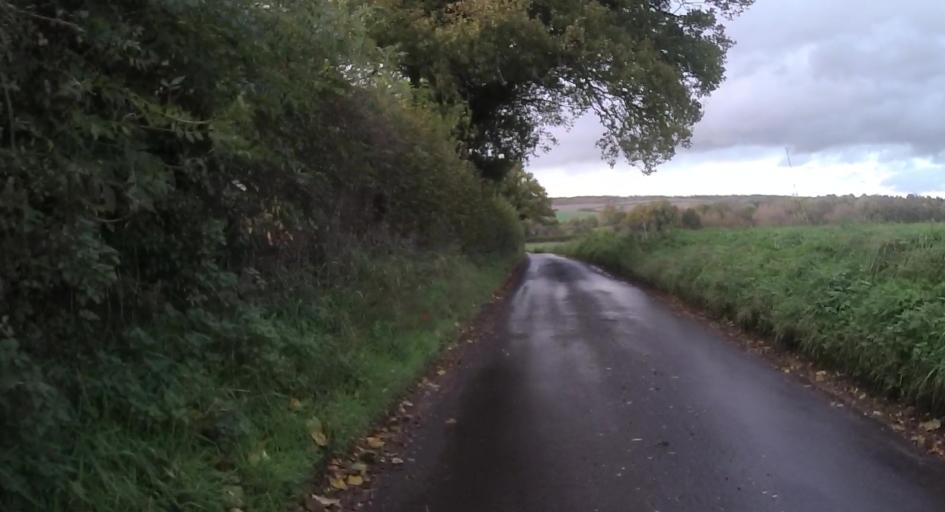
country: GB
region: England
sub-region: Hampshire
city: Alton
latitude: 51.1651
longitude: -0.9264
